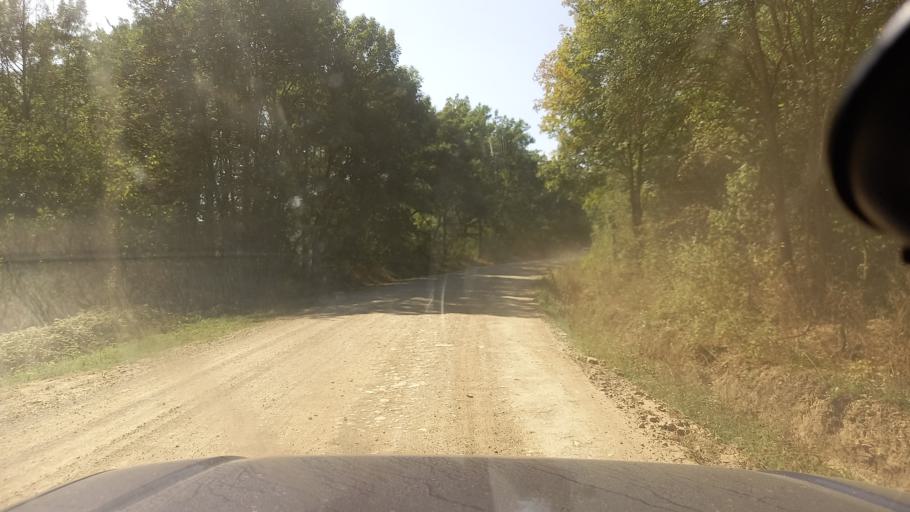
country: RU
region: Krasnodarskiy
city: Azovskaya
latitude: 44.6948
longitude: 38.6434
